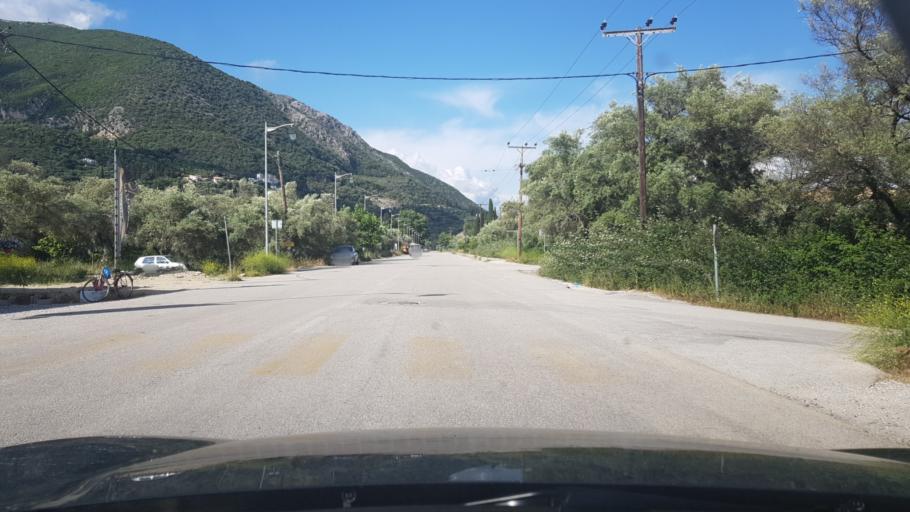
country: GR
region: Ionian Islands
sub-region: Lefkada
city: Nidri
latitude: 38.7097
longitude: 20.7055
